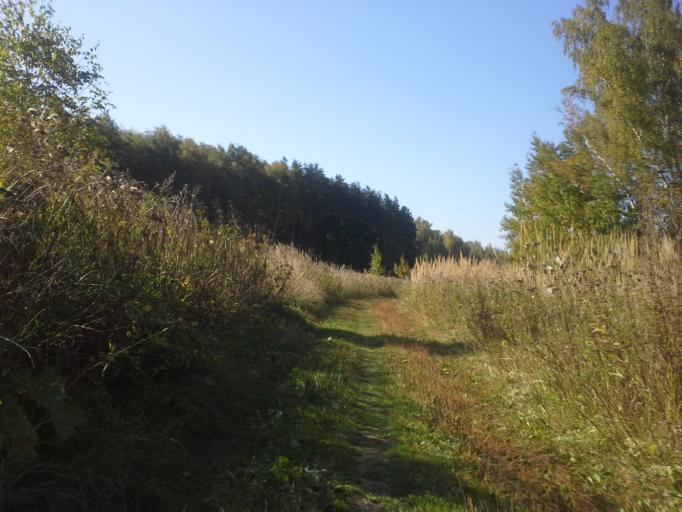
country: RU
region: Moskovskaya
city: Kommunarka
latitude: 55.5481
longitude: 37.4715
